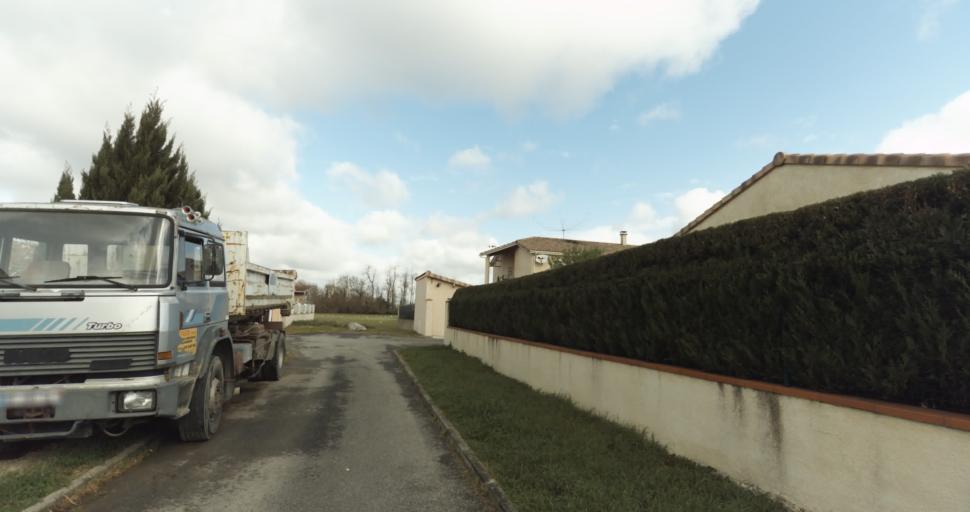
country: FR
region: Midi-Pyrenees
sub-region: Departement de la Haute-Garonne
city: Auterive
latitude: 43.3692
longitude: 1.4524
